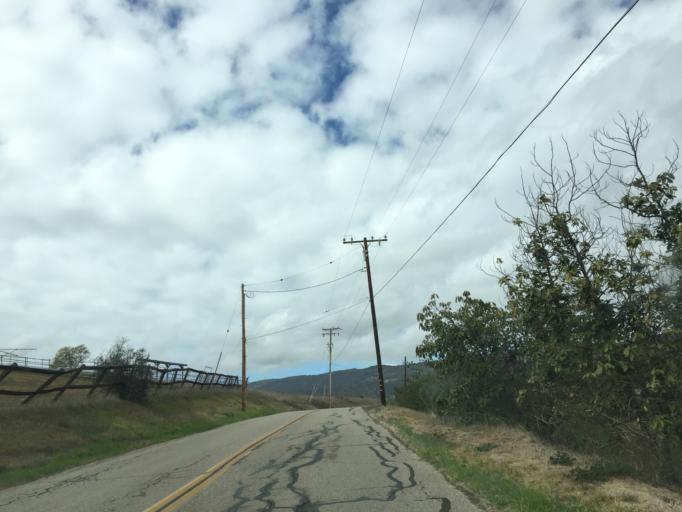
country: US
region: California
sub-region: Santa Barbara County
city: Goleta
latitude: 34.4638
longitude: -119.7994
